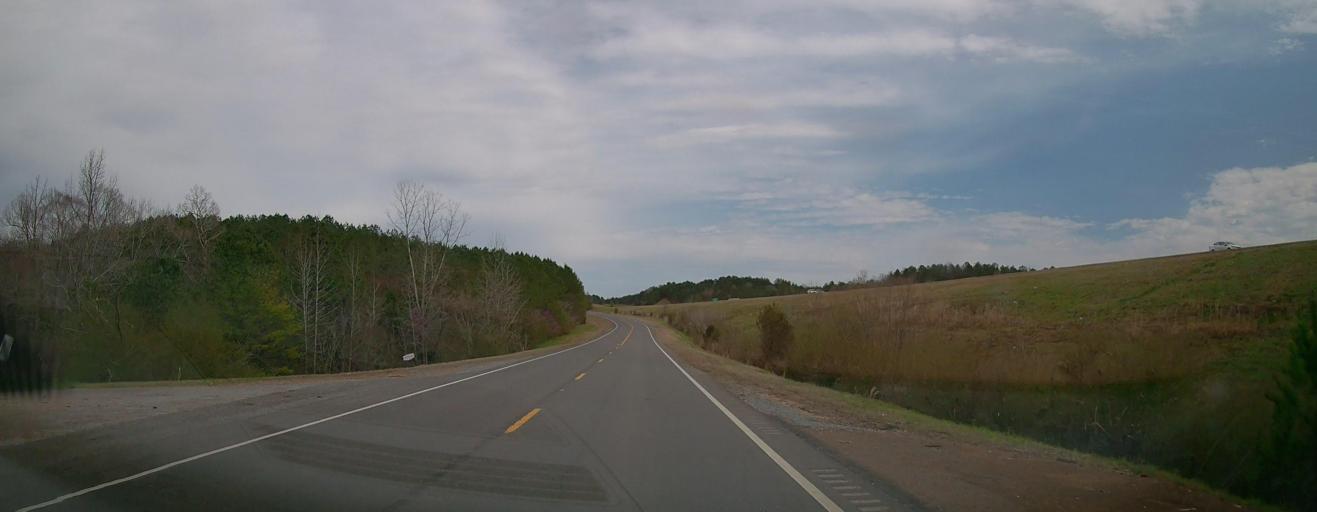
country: US
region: Alabama
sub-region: Walker County
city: Jasper
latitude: 33.8599
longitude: -87.3795
